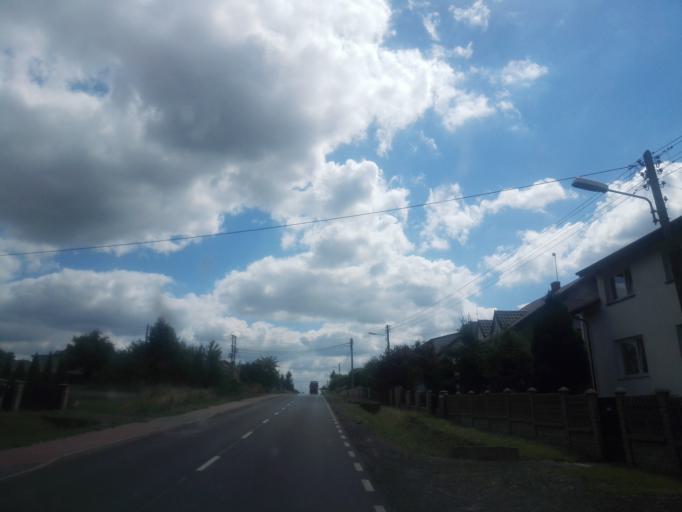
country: PL
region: Silesian Voivodeship
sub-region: Powiat czestochowski
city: Mstow
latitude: 50.7973
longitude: 19.2618
